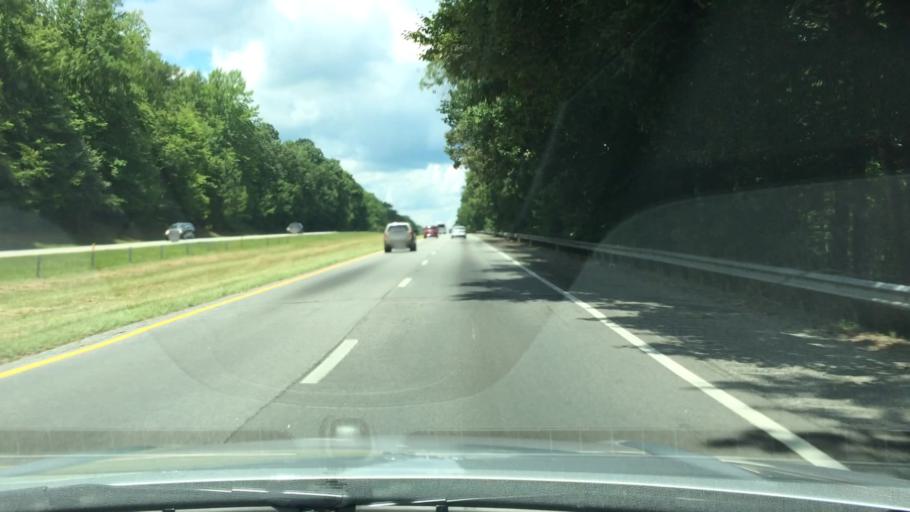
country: US
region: South Carolina
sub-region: Lexington County
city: Chapin
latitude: 34.1954
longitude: -81.3544
